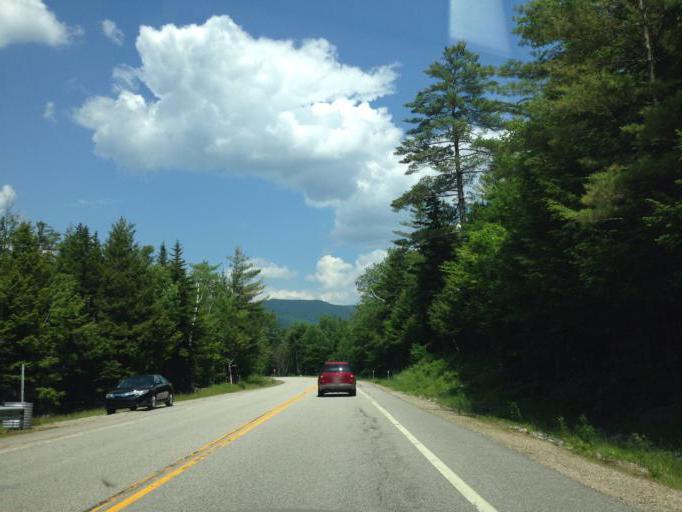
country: US
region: New Hampshire
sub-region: Carroll County
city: Tamworth
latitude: 44.0086
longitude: -71.2709
